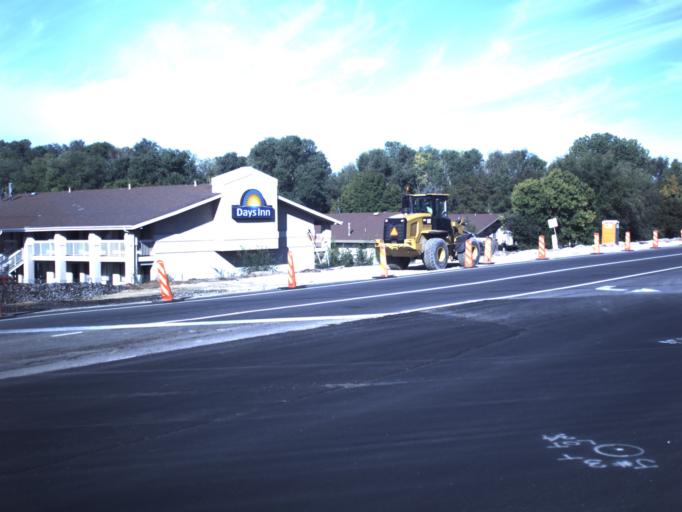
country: US
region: Utah
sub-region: Utah County
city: Provo
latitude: 40.2579
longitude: -111.6618
